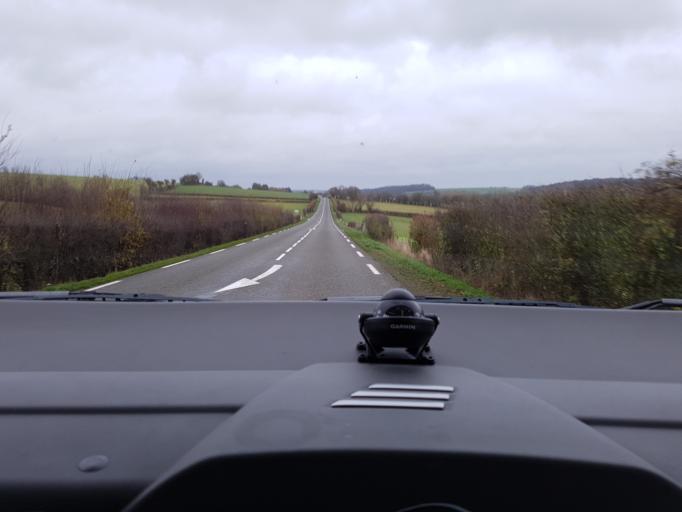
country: FR
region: Picardie
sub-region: Departement de l'Oise
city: Songeons
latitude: 49.5209
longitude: 1.8302
